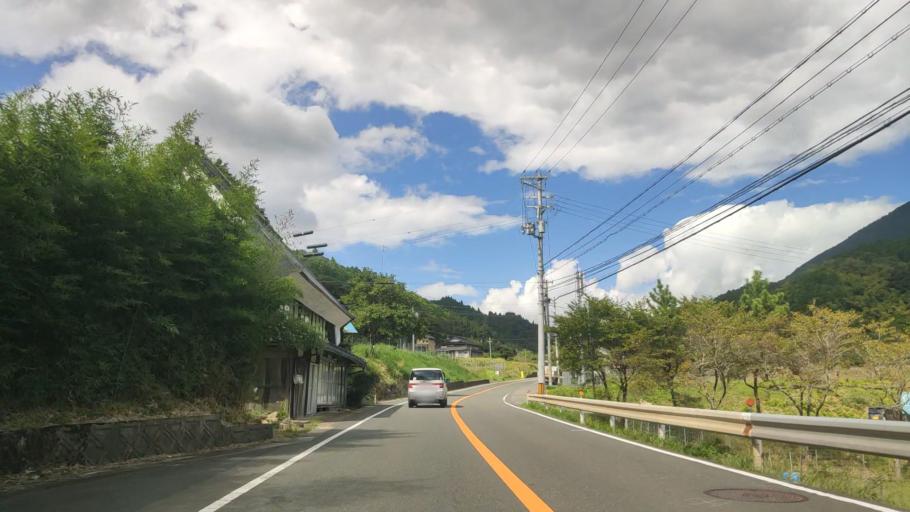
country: JP
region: Kyoto
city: Fukuchiyama
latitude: 35.3719
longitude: 135.0461
